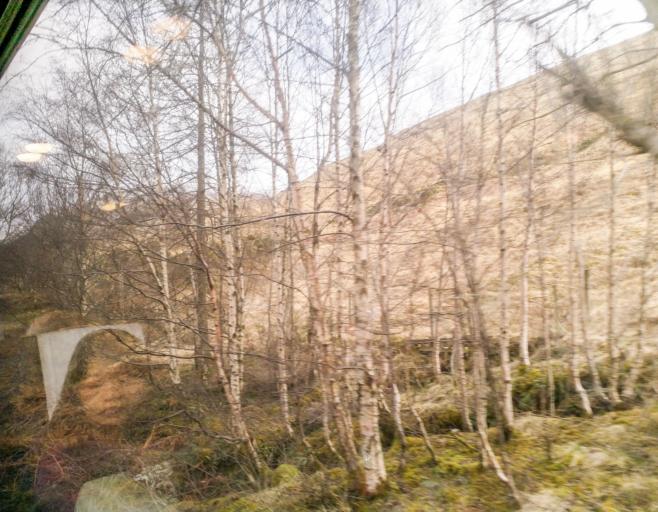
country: GB
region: Scotland
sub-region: Highland
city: Spean Bridge
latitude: 56.8069
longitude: -4.7184
